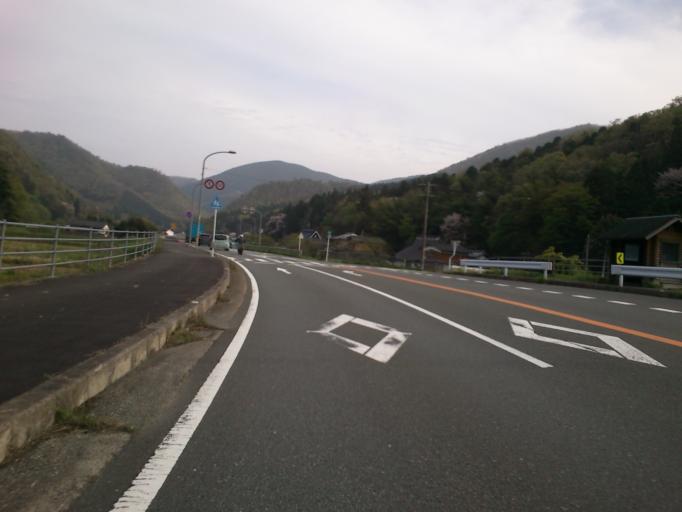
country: JP
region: Hyogo
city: Sasayama
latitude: 35.1629
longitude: 135.3527
